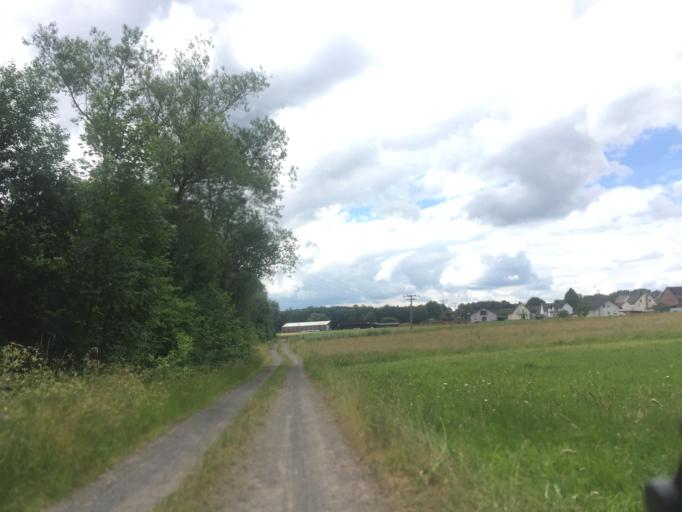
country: DE
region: Rheinland-Pfalz
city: Girod
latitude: 50.4495
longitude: 7.9145
